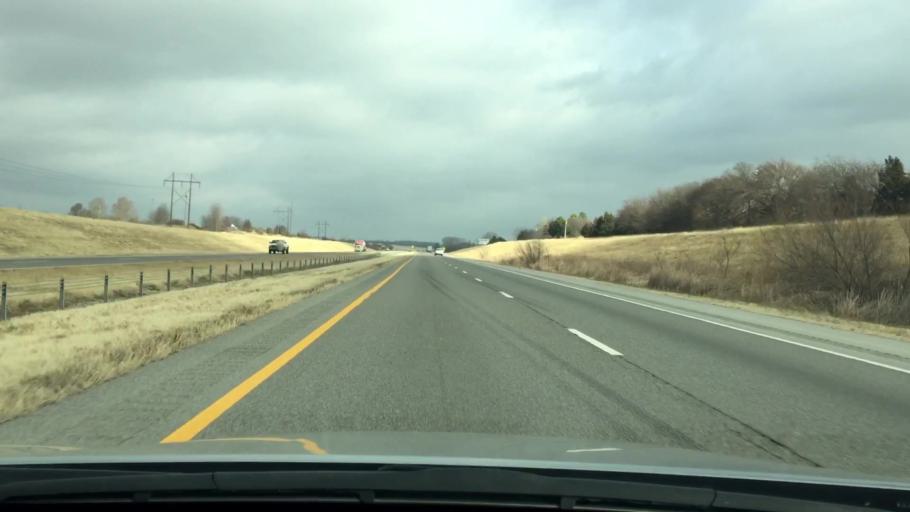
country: US
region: Oklahoma
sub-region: McClain County
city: Purcell
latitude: 35.0226
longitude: -97.3758
